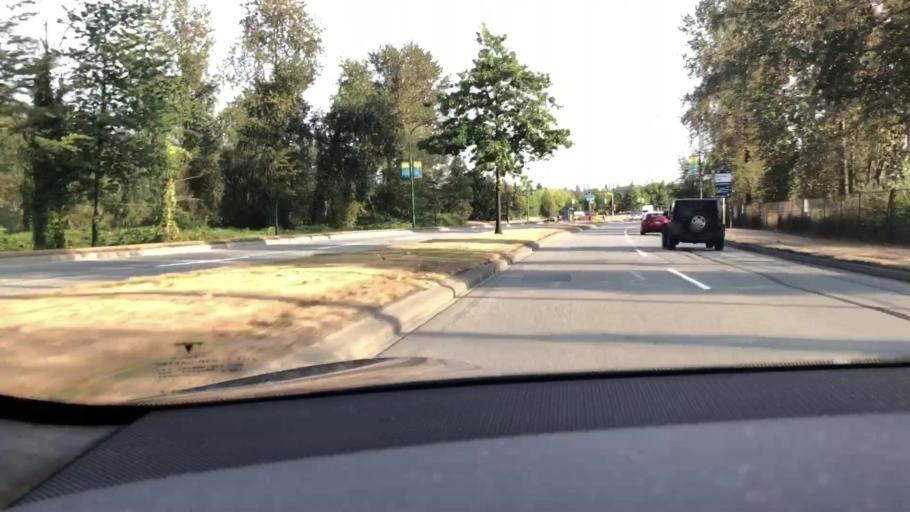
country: CA
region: British Columbia
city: Burnaby
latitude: 49.2552
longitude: -122.9669
